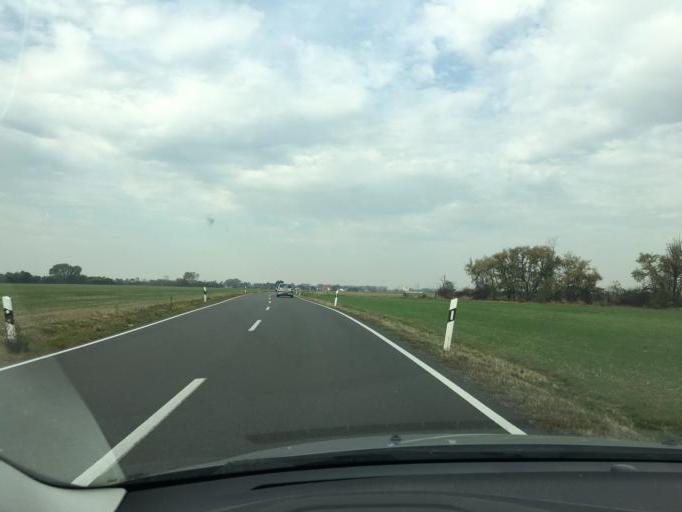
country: DE
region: Saxony
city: Zwochau
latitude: 51.4470
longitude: 12.2719
